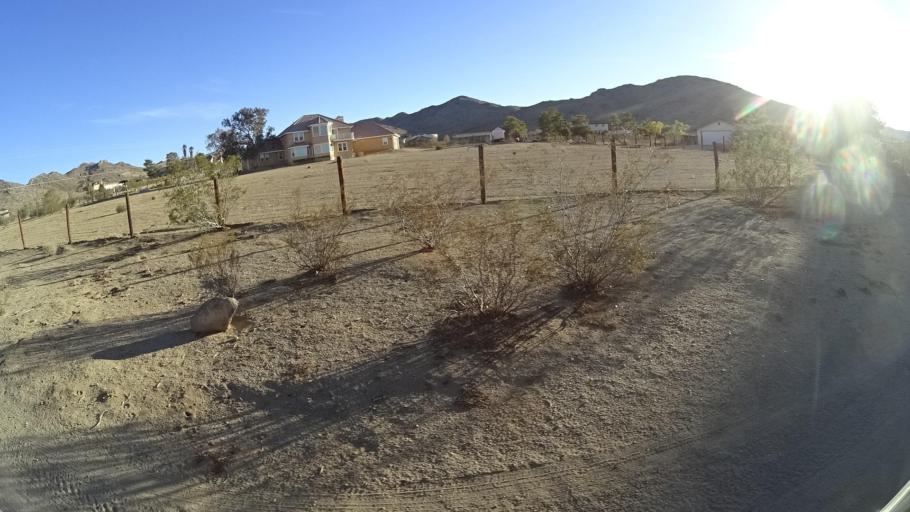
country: US
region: California
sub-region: Kern County
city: Ridgecrest
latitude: 35.5824
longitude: -117.6533
